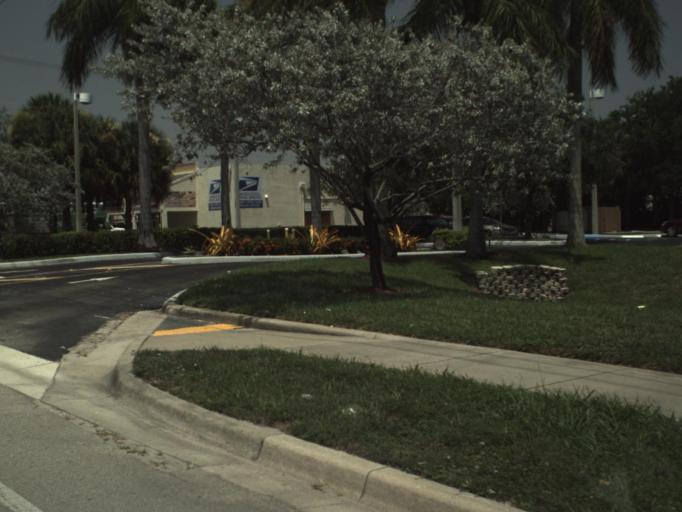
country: US
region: Florida
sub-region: Broward County
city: Tedder
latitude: 26.2722
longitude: -80.1520
